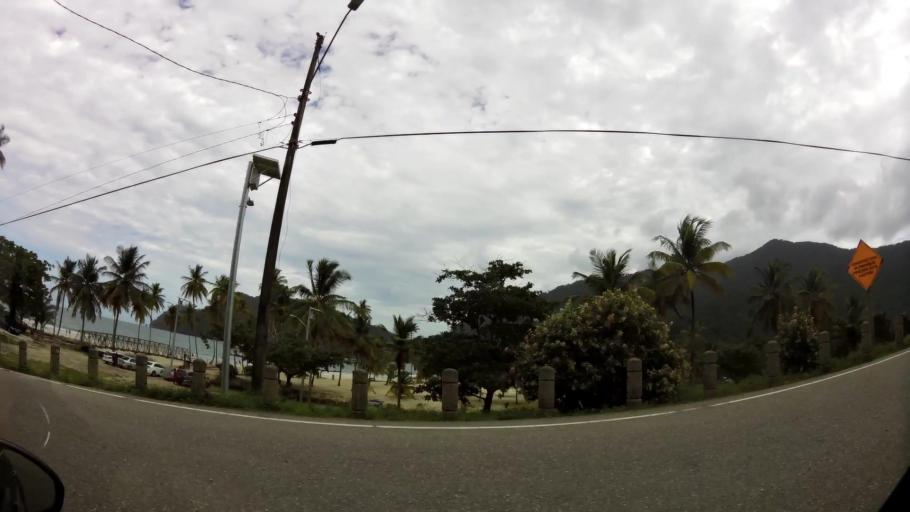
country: TT
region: Diego Martin
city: Petit Valley
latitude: 10.7598
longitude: -61.4427
